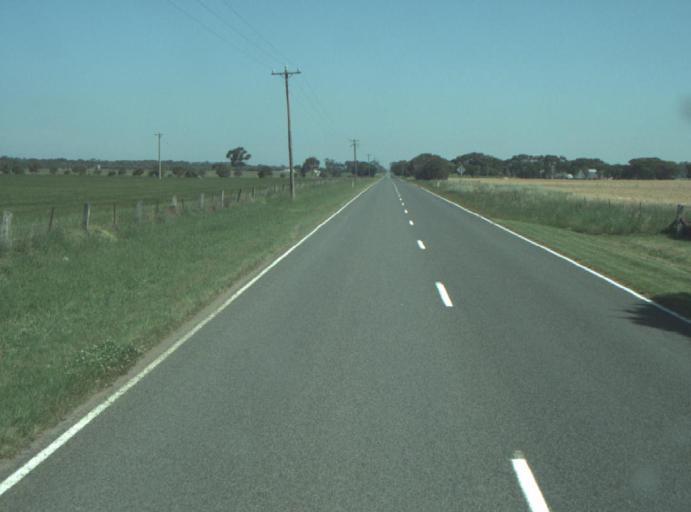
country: AU
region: Victoria
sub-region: Greater Geelong
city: Lara
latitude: -37.9807
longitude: 144.4039
